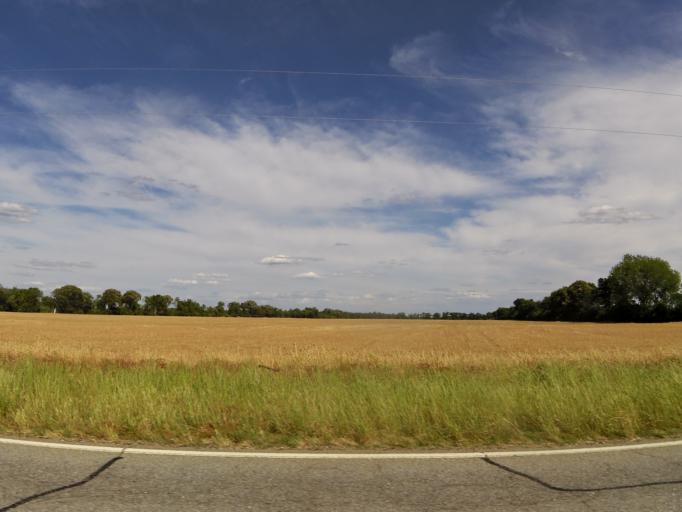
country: US
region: South Carolina
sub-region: Bamberg County
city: Denmark
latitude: 33.1966
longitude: -81.1792
